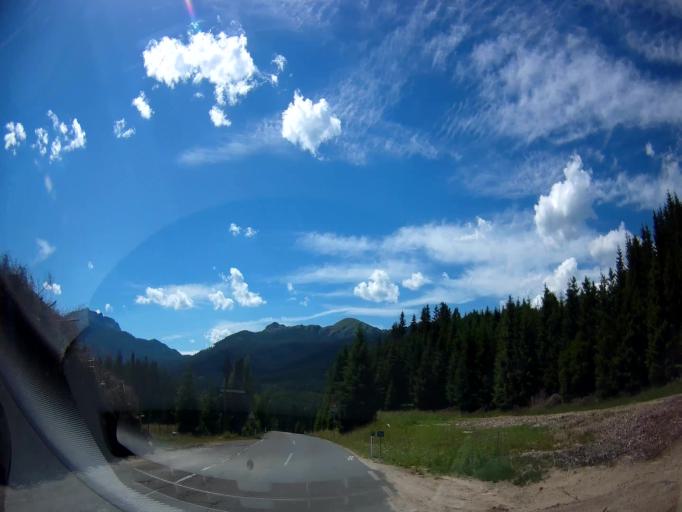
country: AT
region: Styria
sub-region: Politischer Bezirk Murau
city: Stadl an der Mur
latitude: 46.9716
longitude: 14.0152
